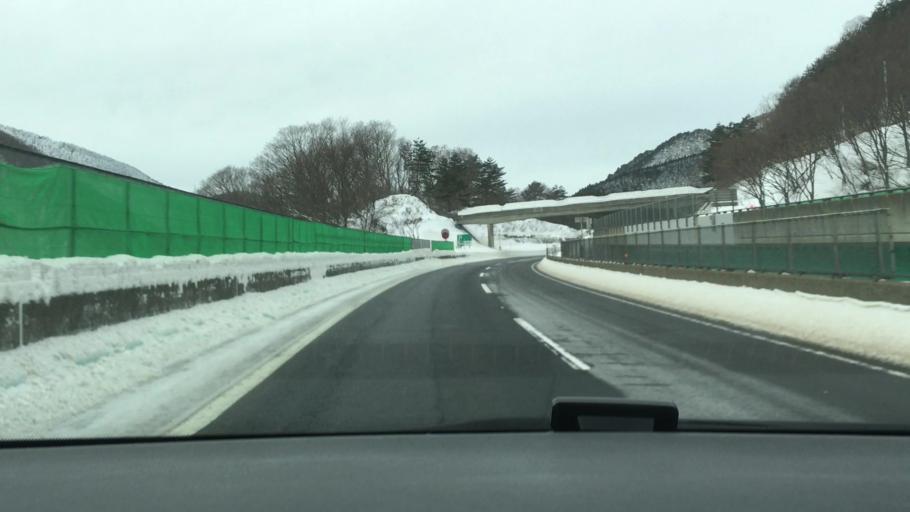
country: JP
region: Akita
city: Hanawa
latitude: 40.1210
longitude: 140.8448
